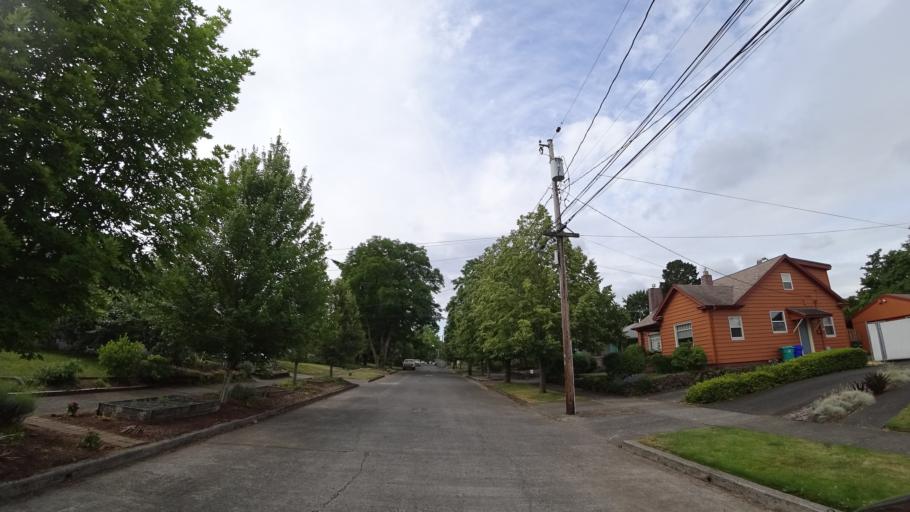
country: US
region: Oregon
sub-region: Multnomah County
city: Portland
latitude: 45.5731
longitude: -122.6843
